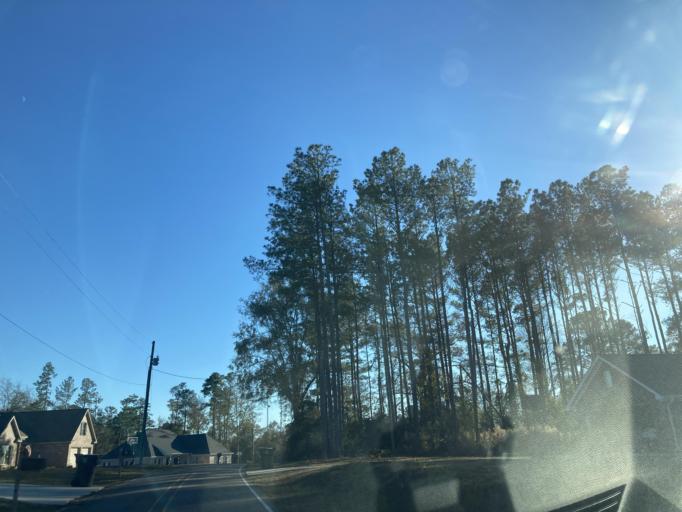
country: US
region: Mississippi
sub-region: Lamar County
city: Sumrall
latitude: 31.4043
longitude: -89.5815
